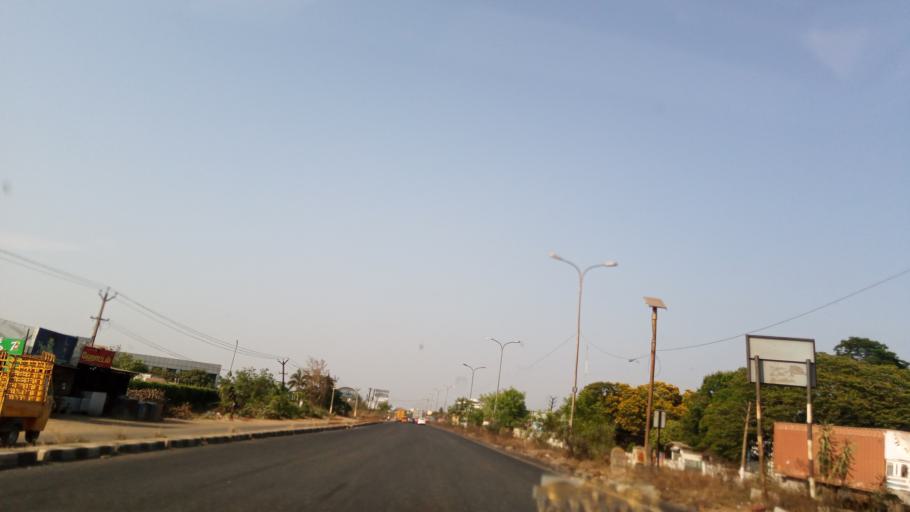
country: IN
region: Tamil Nadu
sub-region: Kancheepuram
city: Sriperumbudur
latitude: 13.0044
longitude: 79.9939
